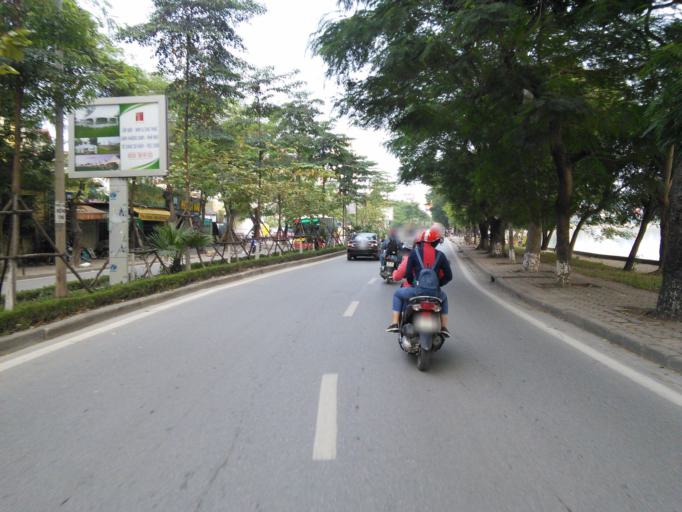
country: VN
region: Ha Noi
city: Van Dien
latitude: 20.9708
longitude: 105.8349
